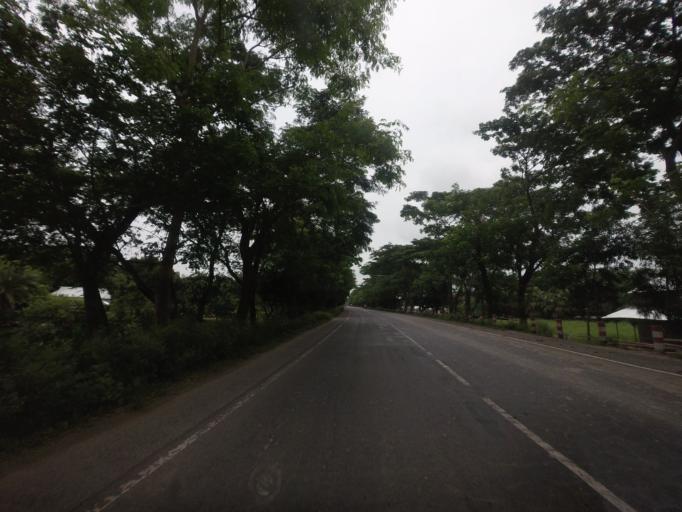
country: BD
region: Khulna
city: Kalia
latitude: 23.2434
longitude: 89.7533
